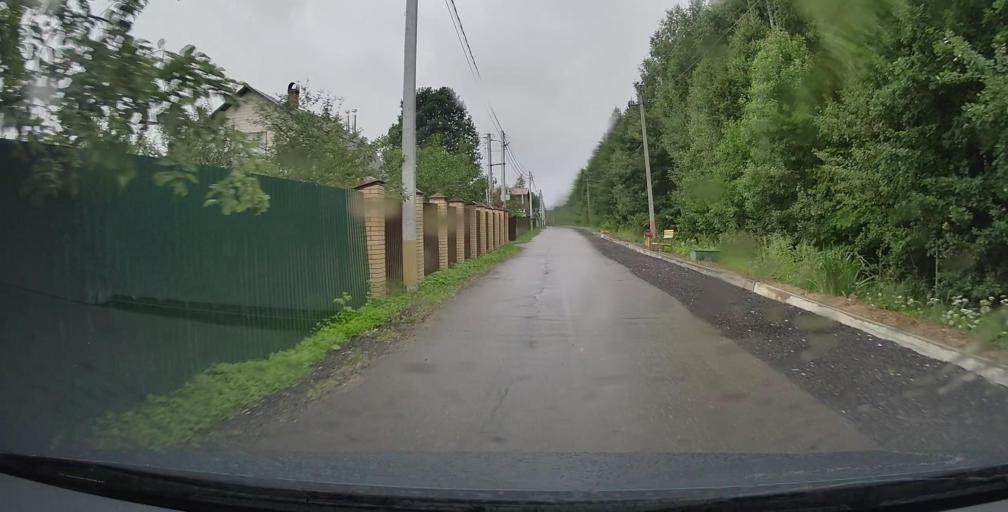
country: RU
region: Moskovskaya
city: Selyatino
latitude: 55.3932
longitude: 37.0176
